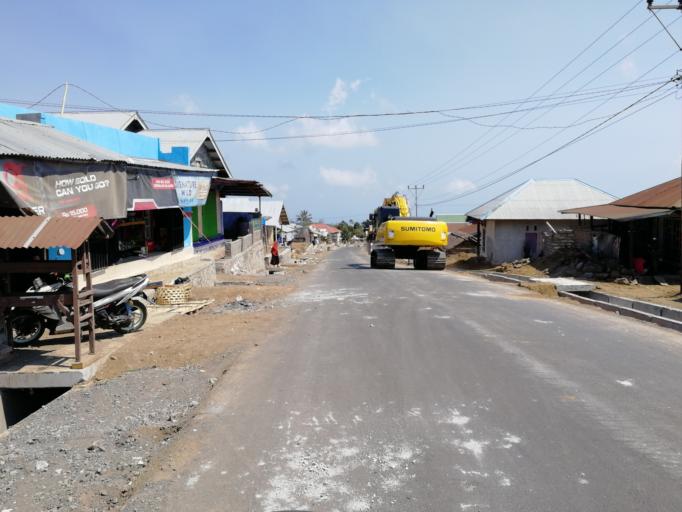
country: ID
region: West Nusa Tenggara
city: Lelongken
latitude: -8.3395
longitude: 116.5007
